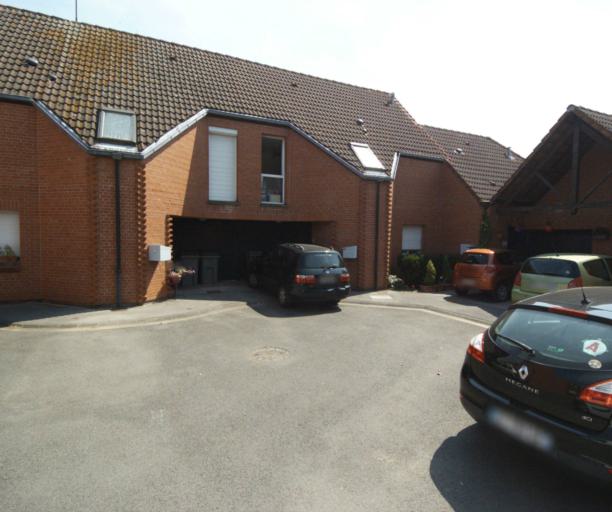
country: FR
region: Nord-Pas-de-Calais
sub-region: Departement du Nord
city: Comines
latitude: 50.7603
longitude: 3.0105
